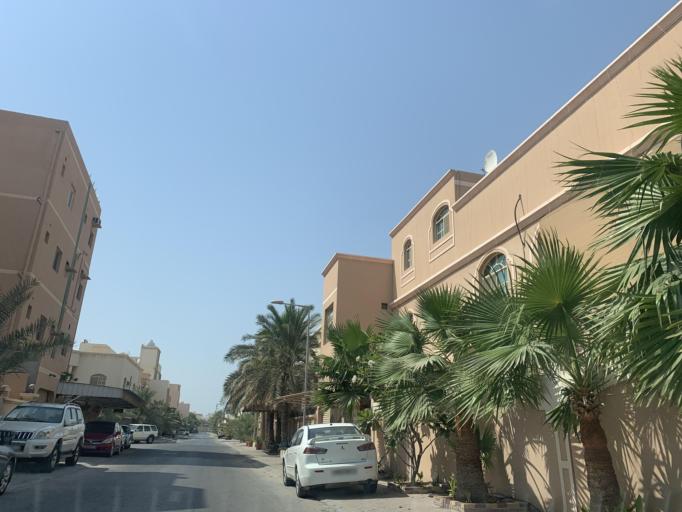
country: BH
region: Manama
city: Jidd Hafs
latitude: 26.2036
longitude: 50.5230
